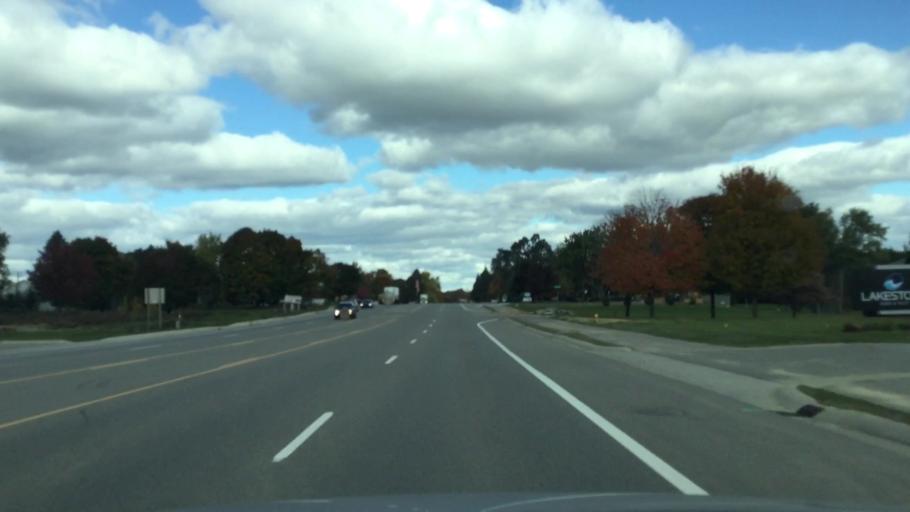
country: US
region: Michigan
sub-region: Lapeer County
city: Lapeer
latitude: 43.0299
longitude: -83.3228
